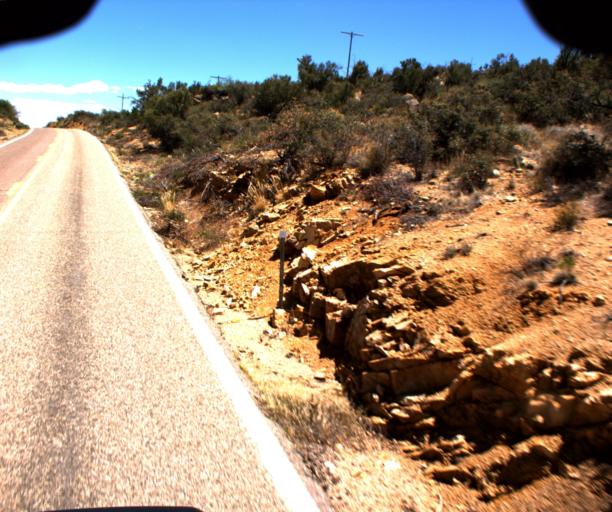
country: US
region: Arizona
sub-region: Yavapai County
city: Bagdad
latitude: 34.4432
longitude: -112.9475
